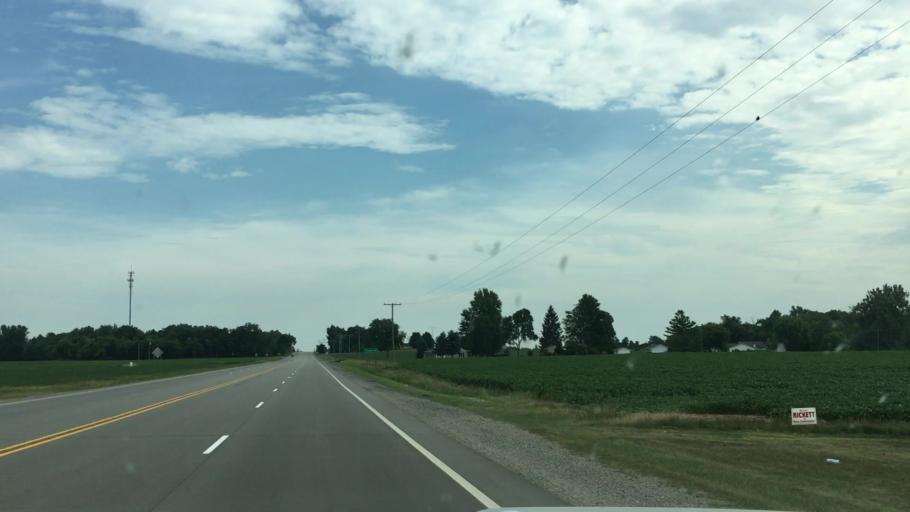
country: US
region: Michigan
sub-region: Sanilac County
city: Marlette
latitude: 43.3889
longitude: -83.0863
